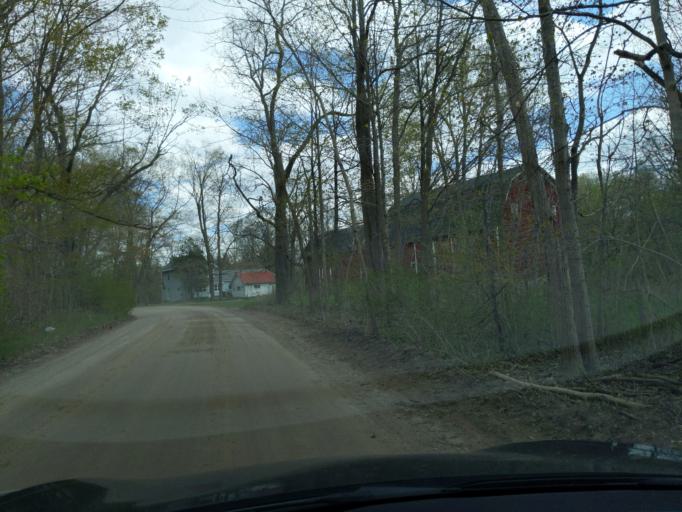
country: US
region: Michigan
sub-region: Eaton County
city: Dimondale
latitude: 42.6260
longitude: -84.6047
